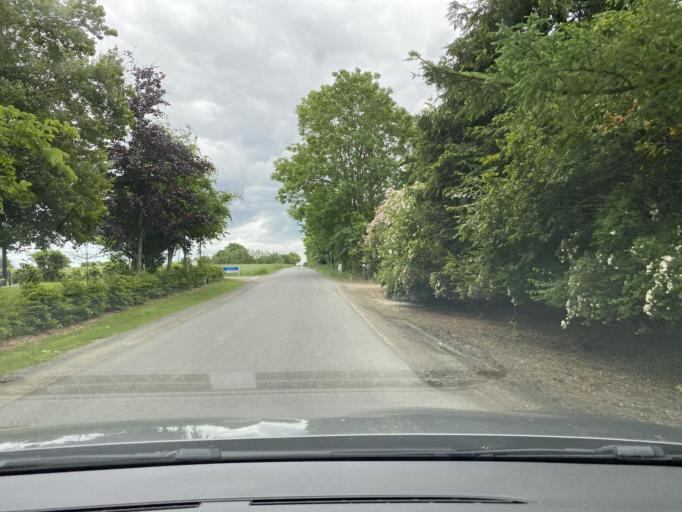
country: DK
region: South Denmark
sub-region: Vejle Kommune
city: Vejle
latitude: 55.6663
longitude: 9.4559
